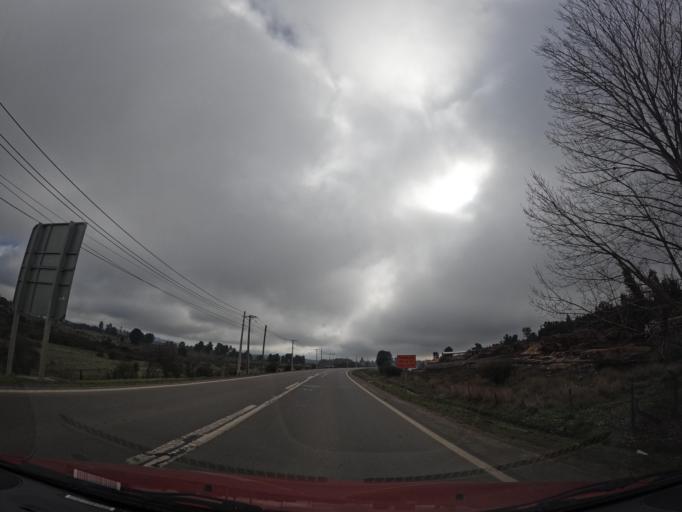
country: CL
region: Maule
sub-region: Provincia de Cauquenes
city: Cauquenes
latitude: -36.2687
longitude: -72.5471
